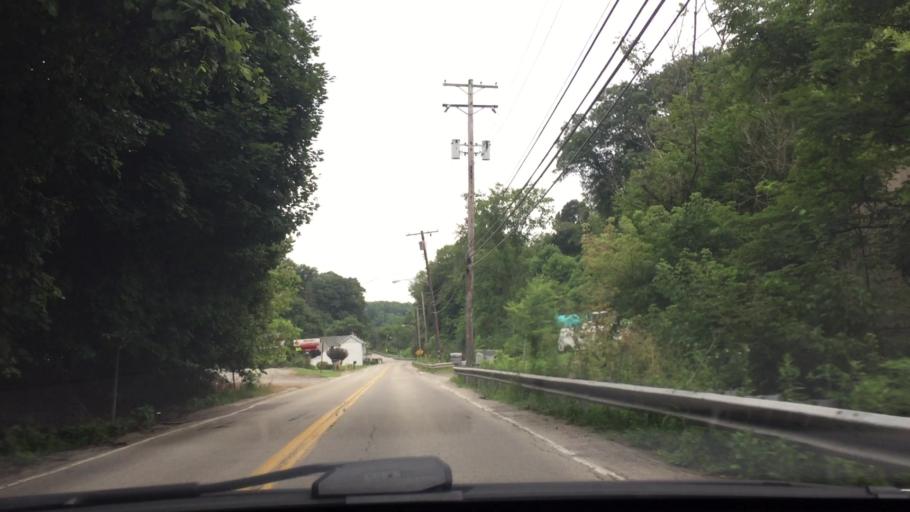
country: US
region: Pennsylvania
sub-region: Allegheny County
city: Rennerdale
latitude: 40.3788
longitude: -80.1473
